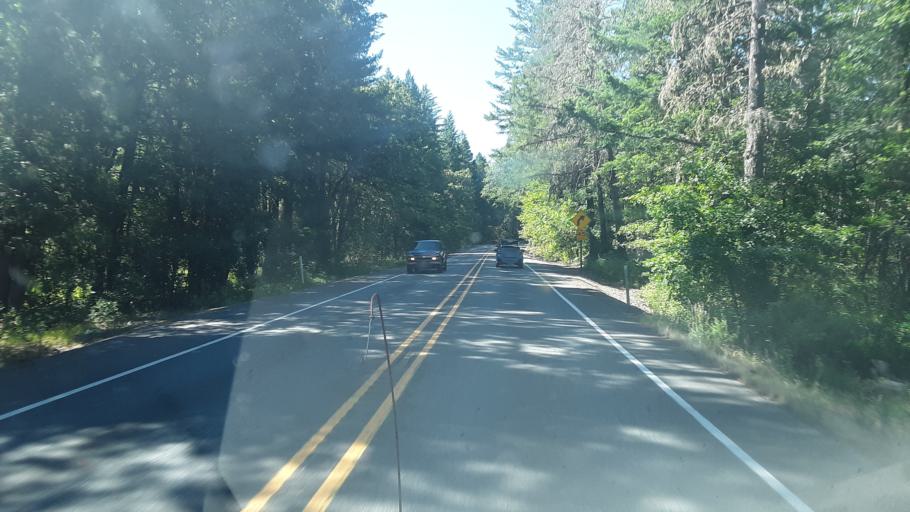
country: US
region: Oregon
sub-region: Josephine County
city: Cave Junction
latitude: 42.2595
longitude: -123.6187
